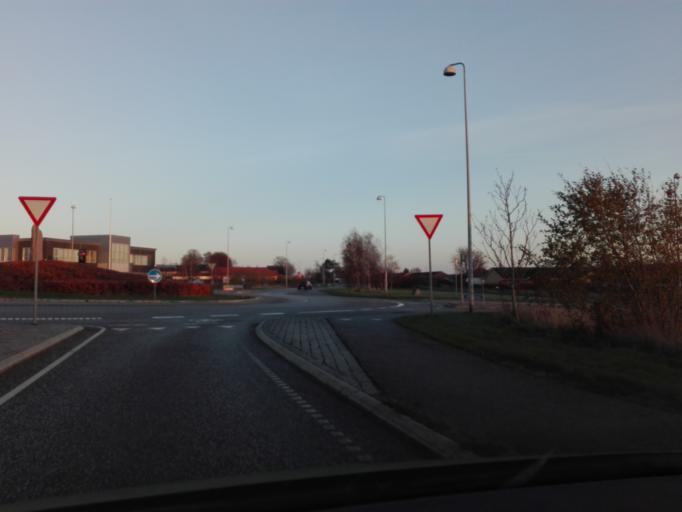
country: DK
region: Central Jutland
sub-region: Arhus Kommune
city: Framlev
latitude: 56.1519
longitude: 9.9993
